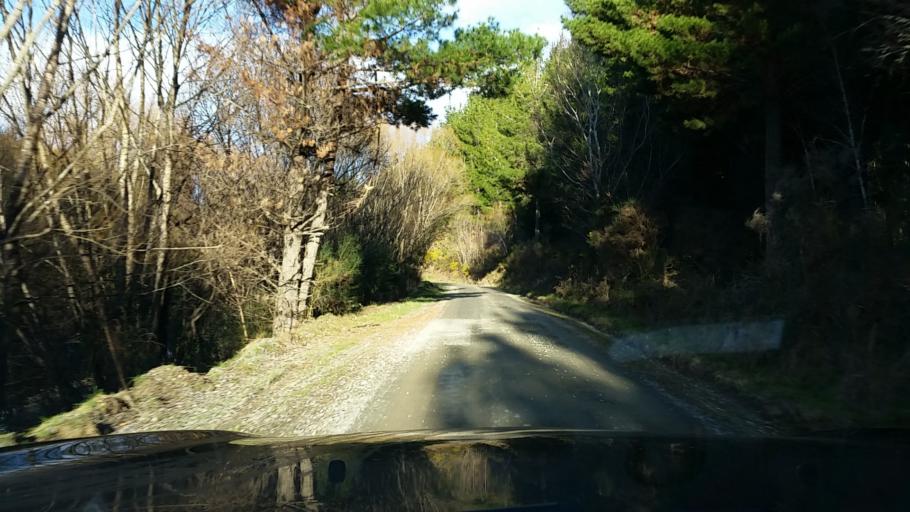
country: NZ
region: Nelson
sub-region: Nelson City
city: Nelson
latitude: -41.5541
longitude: 173.4249
